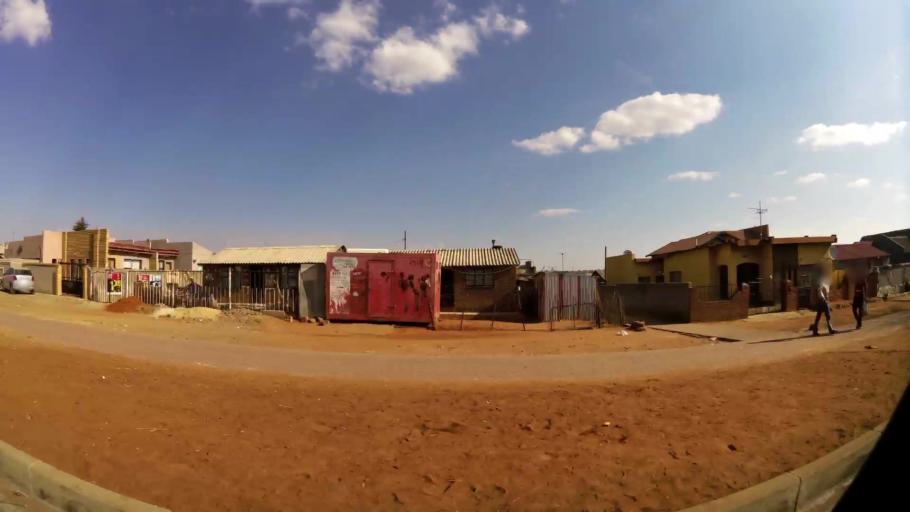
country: ZA
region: Gauteng
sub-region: City of Johannesburg Metropolitan Municipality
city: Roodepoort
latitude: -26.2153
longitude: 27.8843
